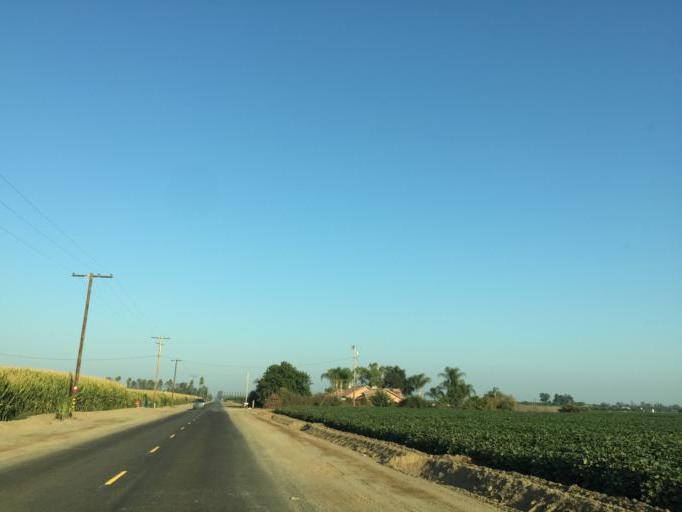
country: US
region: California
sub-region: Tulare County
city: Visalia
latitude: 36.3710
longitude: -119.2687
